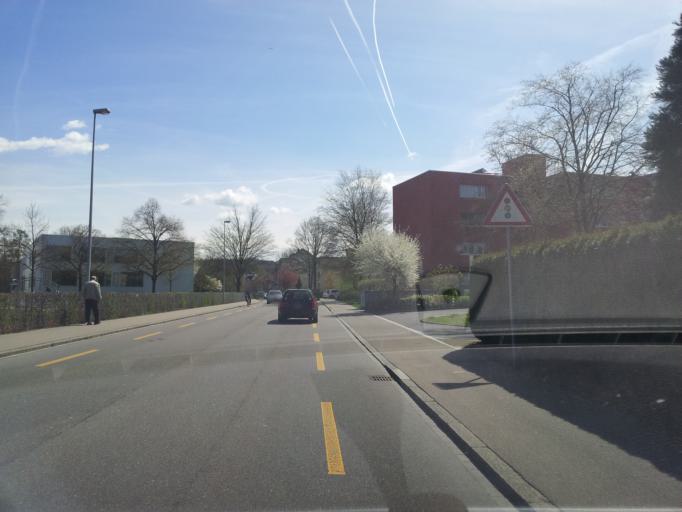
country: CH
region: Zurich
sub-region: Bezirk Dietikon
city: Dietikon / Almend
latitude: 47.4053
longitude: 8.3933
